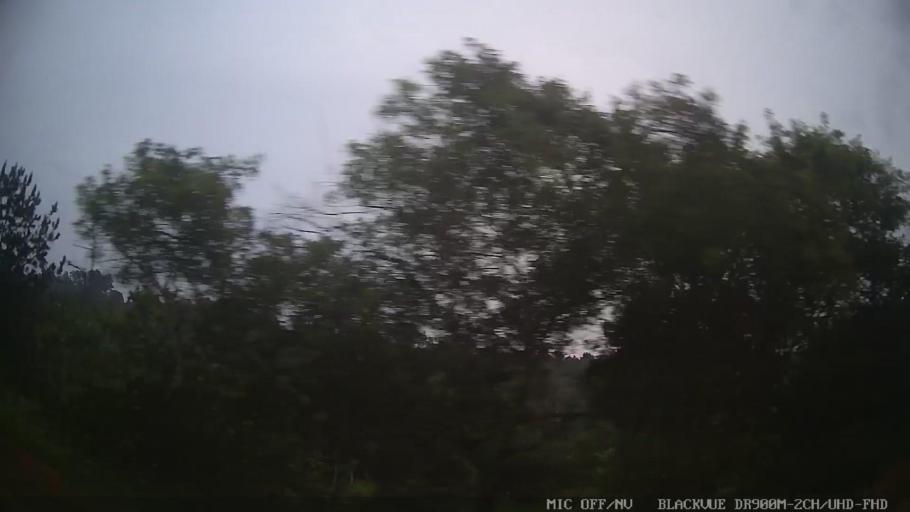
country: BR
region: Sao Paulo
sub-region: Rio Grande Da Serra
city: Rio Grande da Serra
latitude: -23.6897
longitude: -46.3045
